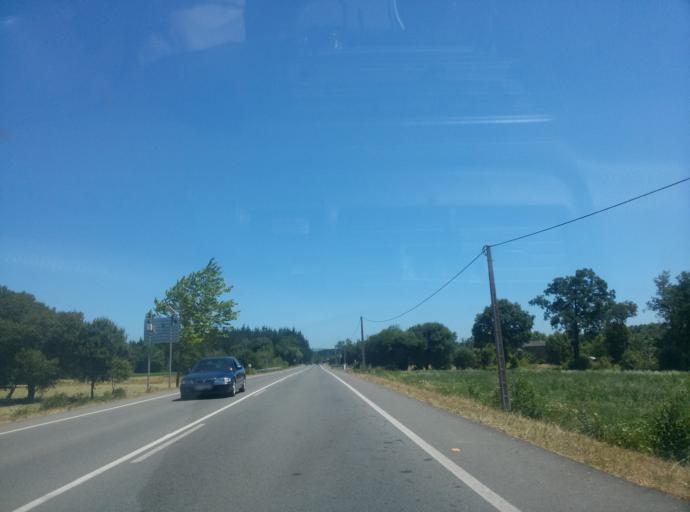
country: ES
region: Galicia
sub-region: Provincia de Lugo
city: Castro de Rei
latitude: 43.2503
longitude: -7.4219
